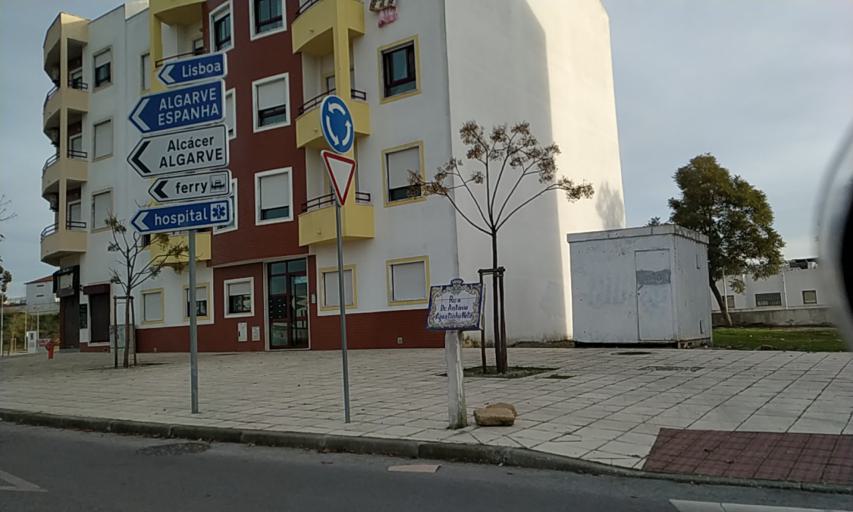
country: PT
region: Setubal
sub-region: Setubal
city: Setubal
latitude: 38.5355
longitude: -8.8788
